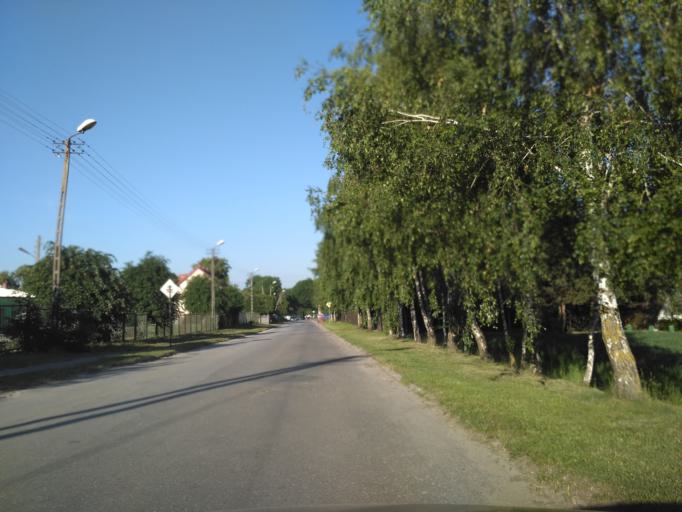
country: PL
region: Lublin Voivodeship
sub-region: Powiat lubelski
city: Bychawa
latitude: 51.0250
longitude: 22.5194
